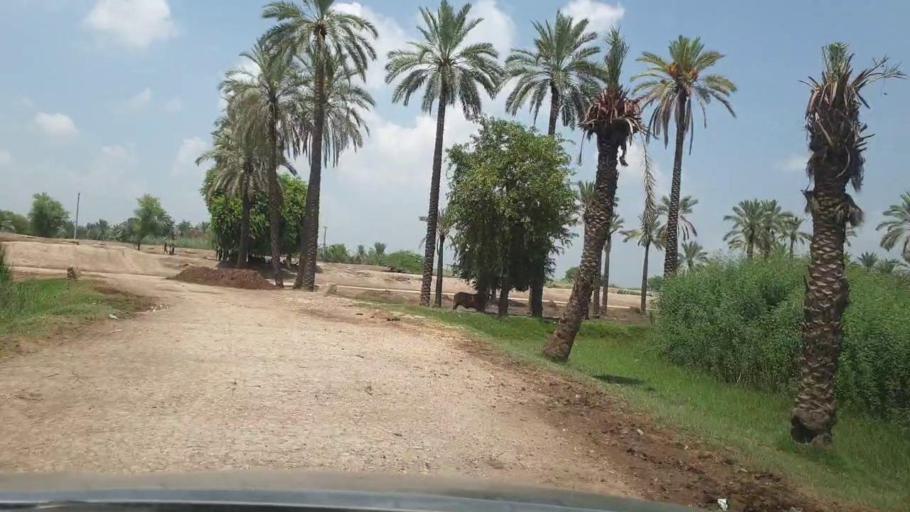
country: PK
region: Sindh
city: Pir jo Goth
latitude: 27.6130
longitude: 68.6041
